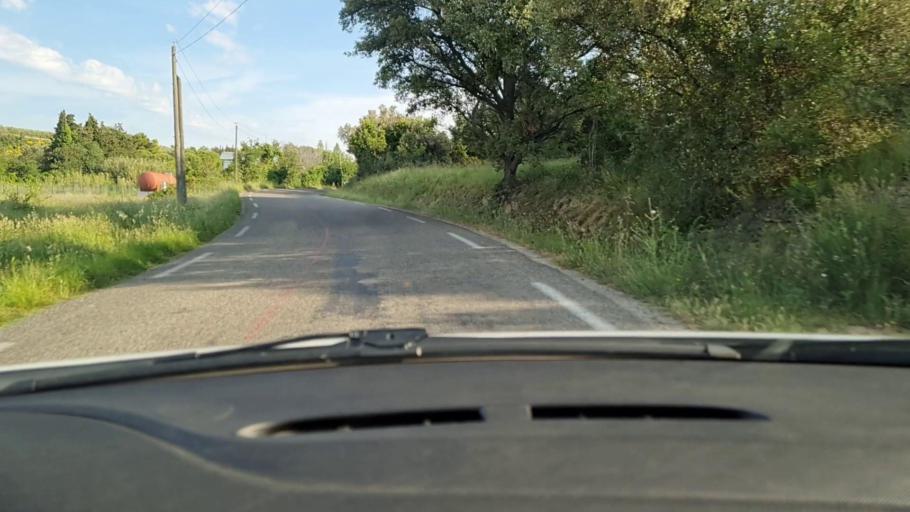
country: FR
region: Languedoc-Roussillon
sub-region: Departement du Gard
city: Bellegarde
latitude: 43.7623
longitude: 4.5102
